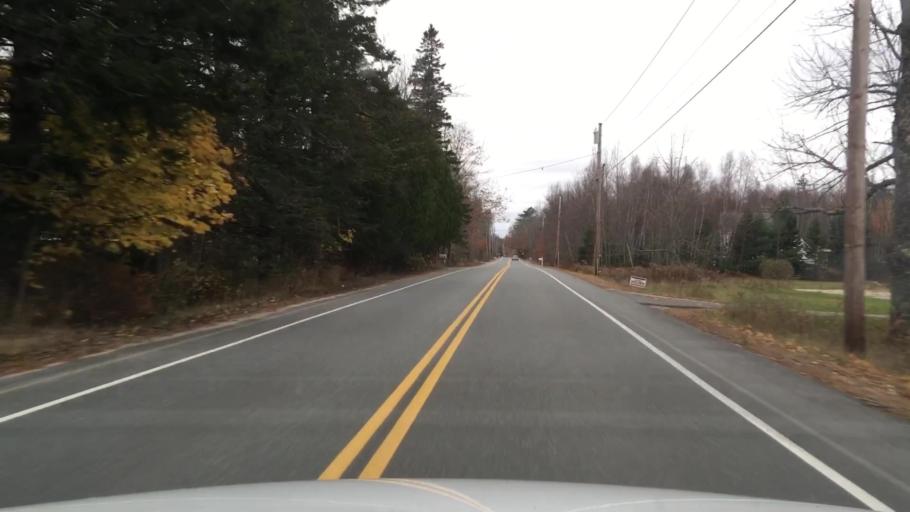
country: US
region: Maine
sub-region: Hancock County
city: Sedgwick
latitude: 44.4116
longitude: -68.6032
